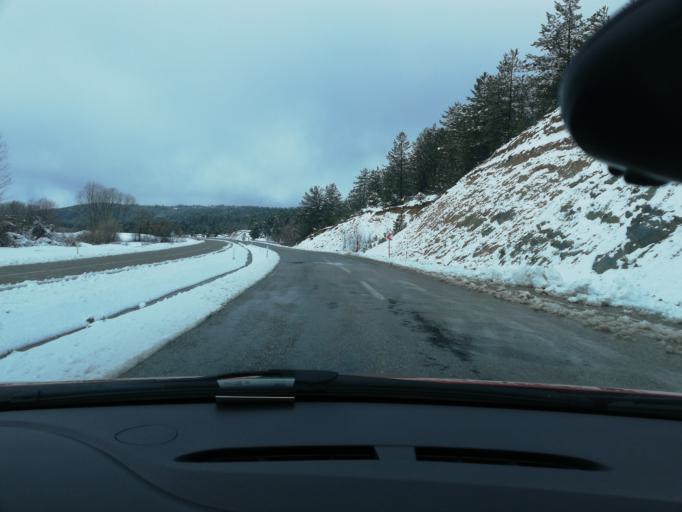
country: TR
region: Kastamonu
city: Akkaya
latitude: 41.2871
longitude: 33.4437
